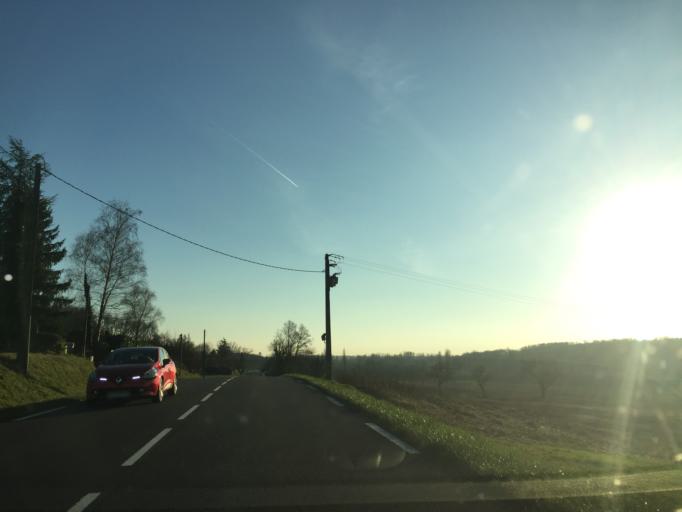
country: FR
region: Poitou-Charentes
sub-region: Departement de la Charente
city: Chalais
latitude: 45.2389
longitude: 0.0376
